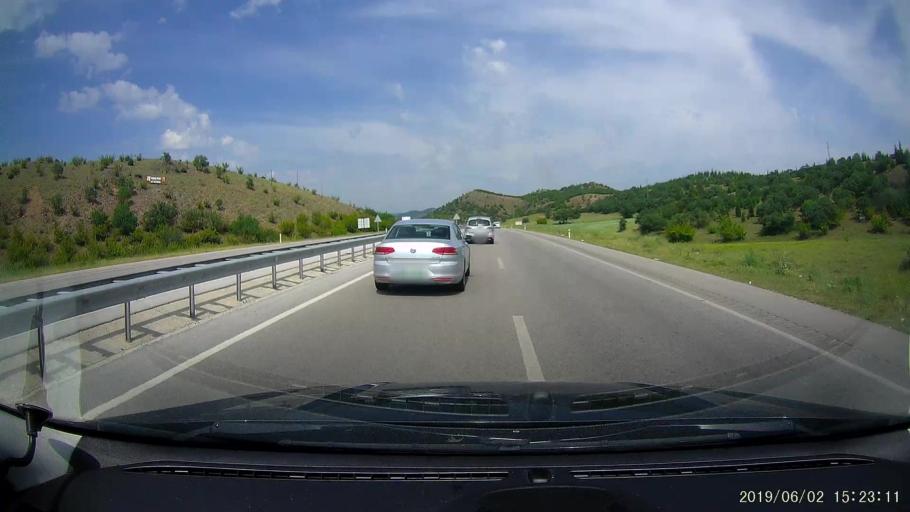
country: TR
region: Corum
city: Osmancik
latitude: 40.9891
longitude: 34.9728
